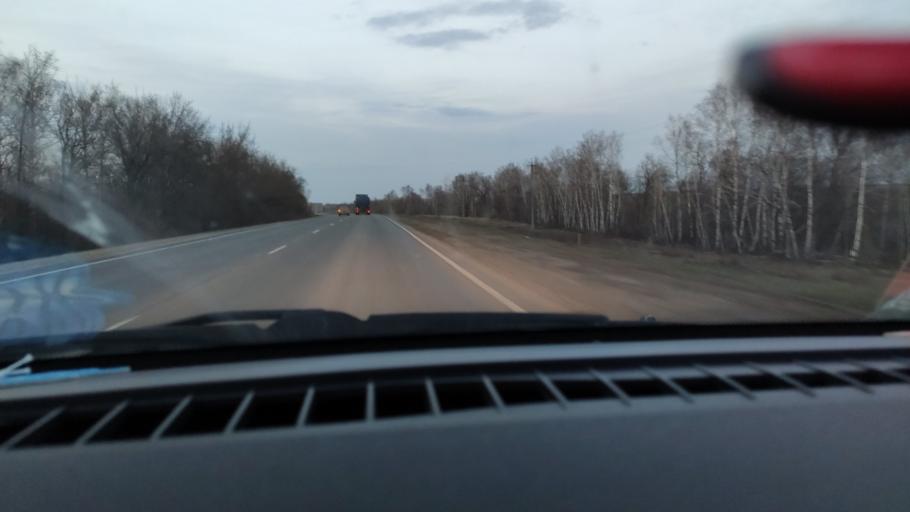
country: RU
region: Saratov
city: Sinodskoye
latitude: 52.0286
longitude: 46.7186
